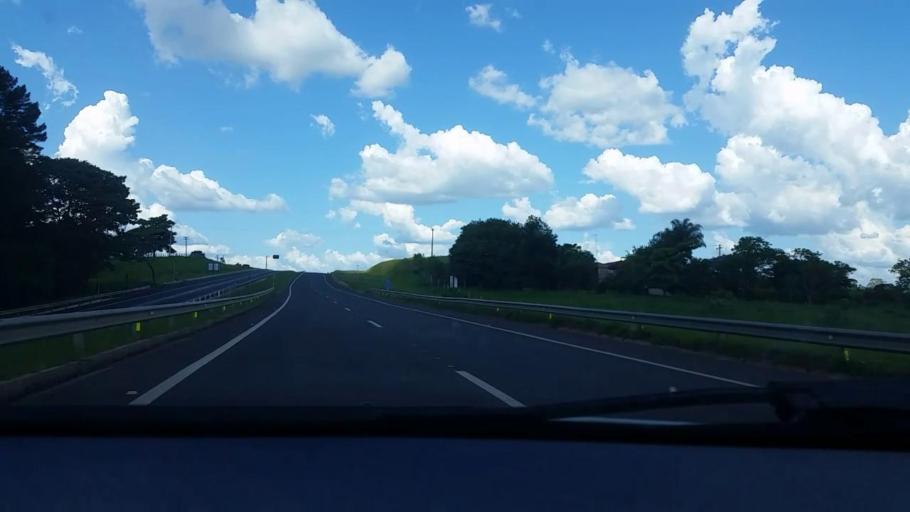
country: BR
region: Sao Paulo
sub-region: Bauru
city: Bauru
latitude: -22.4442
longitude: -49.1547
